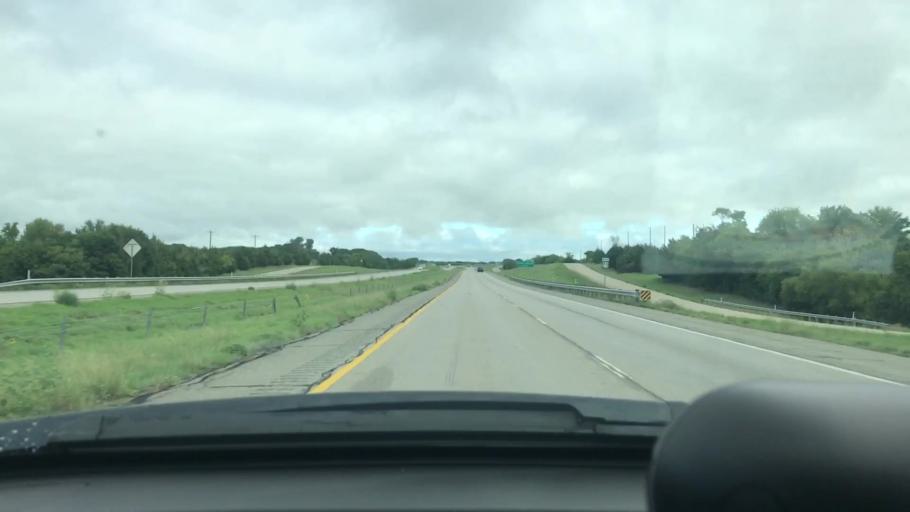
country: US
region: Texas
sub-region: Grayson County
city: Van Alstyne
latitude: 33.3876
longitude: -96.5807
